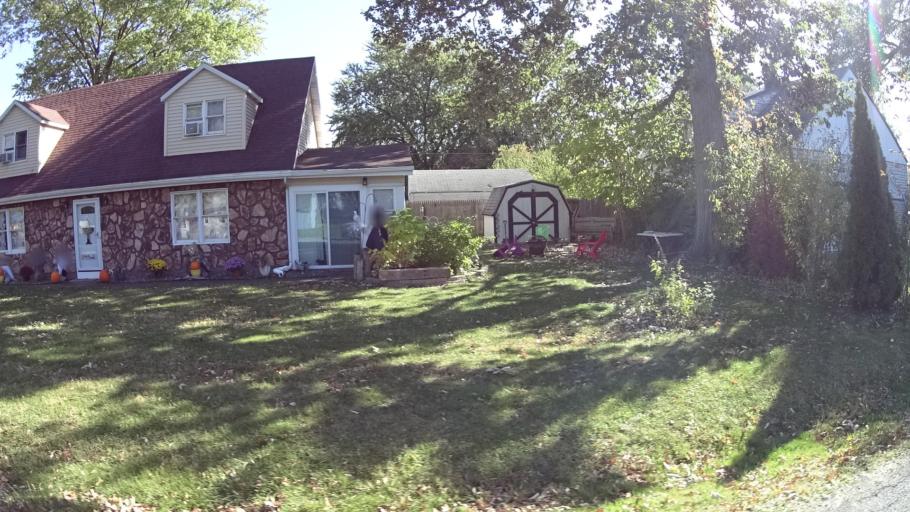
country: US
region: Ohio
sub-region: Lorain County
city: Vermilion-on-the-Lake
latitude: 41.4292
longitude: -82.3257
